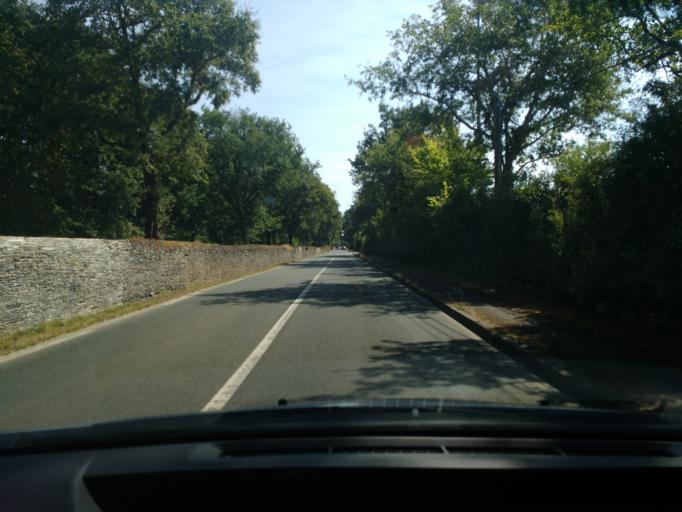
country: FR
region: Pays de la Loire
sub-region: Departement de Maine-et-Loire
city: Trelaze
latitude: 47.4669
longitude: -0.4822
